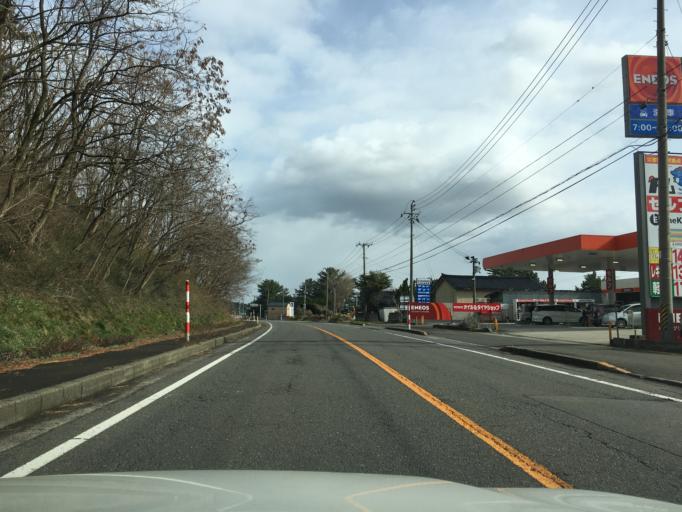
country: JP
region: Yamagata
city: Yuza
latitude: 39.2335
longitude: 139.9093
